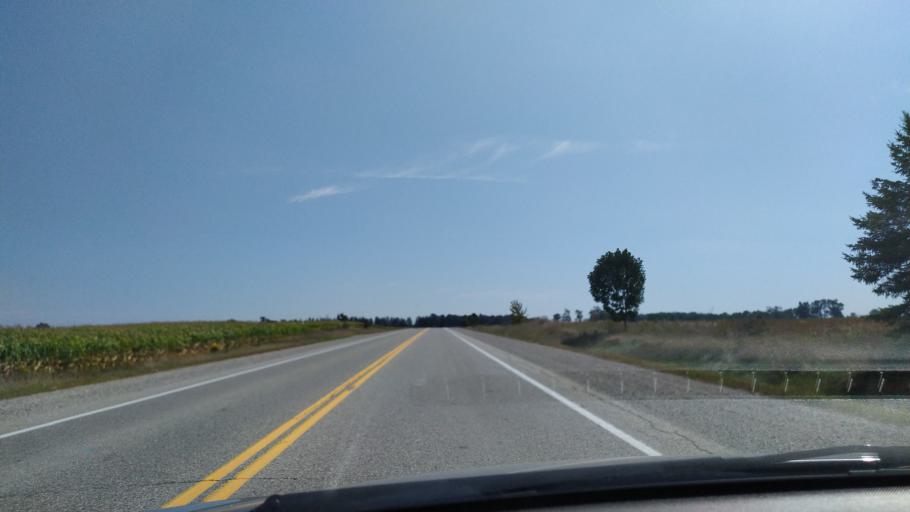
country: CA
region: Ontario
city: Ingersoll
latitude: 43.0922
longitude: -80.8692
